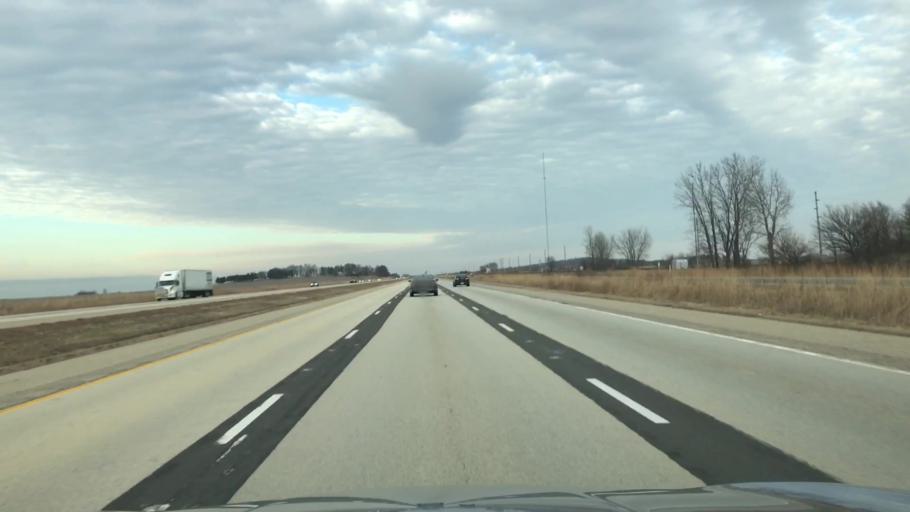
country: US
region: Illinois
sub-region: Sangamon County
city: Williamsville
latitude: 39.9828
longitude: -89.5216
